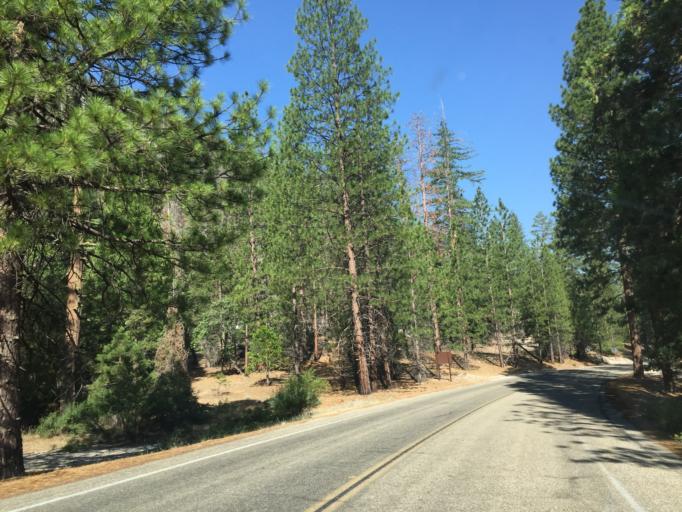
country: US
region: California
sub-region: Tulare County
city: Three Rivers
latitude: 36.7845
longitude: -118.6613
